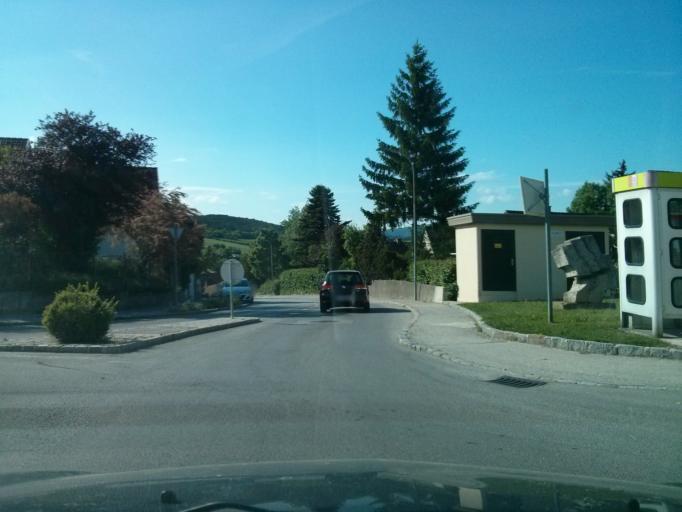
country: AT
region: Lower Austria
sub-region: Politischer Bezirk Baden
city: Hirtenberg
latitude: 47.9181
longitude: 16.1883
